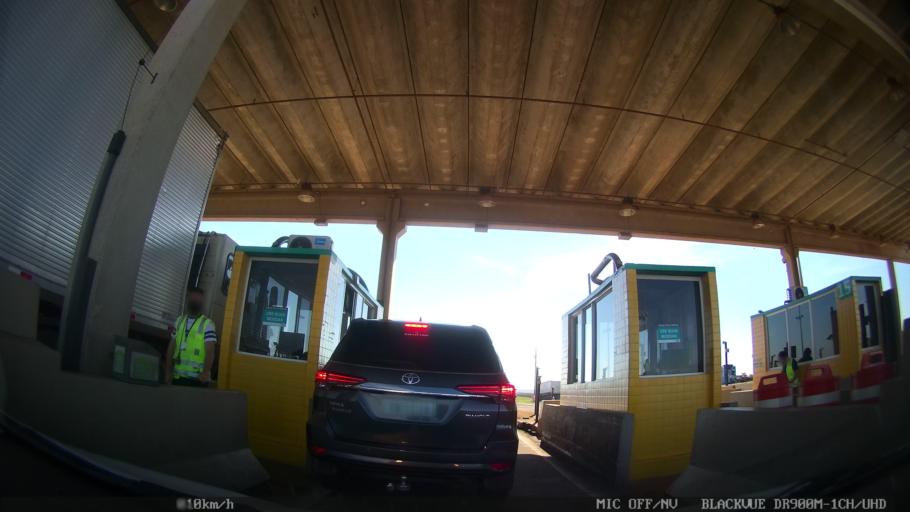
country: BR
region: Sao Paulo
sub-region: Santa Rita Do Passa Quatro
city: Santa Rita do Passa Quatro
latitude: -21.6585
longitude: -47.6089
